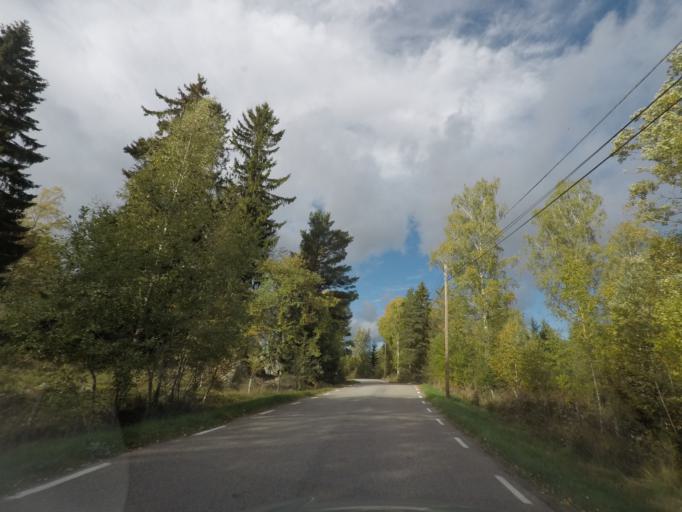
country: SE
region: Soedermanland
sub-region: Eskilstuna Kommun
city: Kvicksund
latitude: 59.3194
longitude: 16.2687
